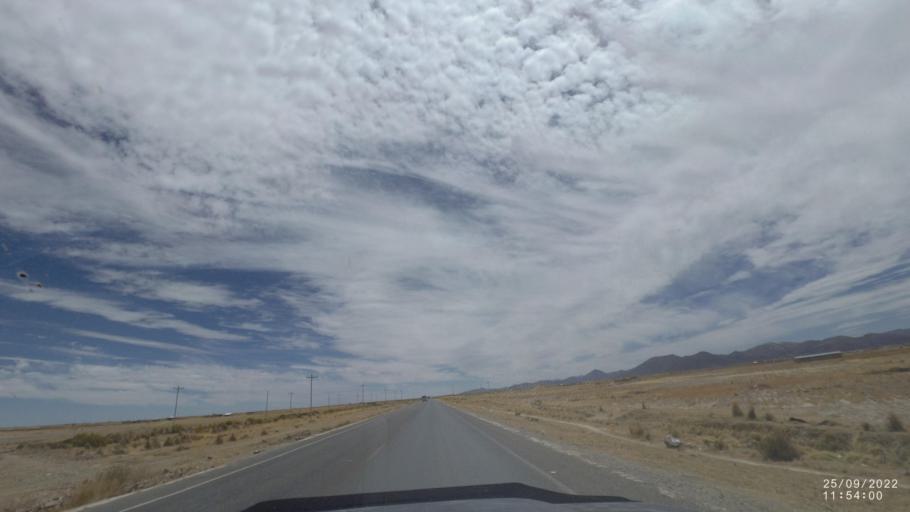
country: BO
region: Oruro
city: Challapata
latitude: -18.8811
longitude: -66.7889
